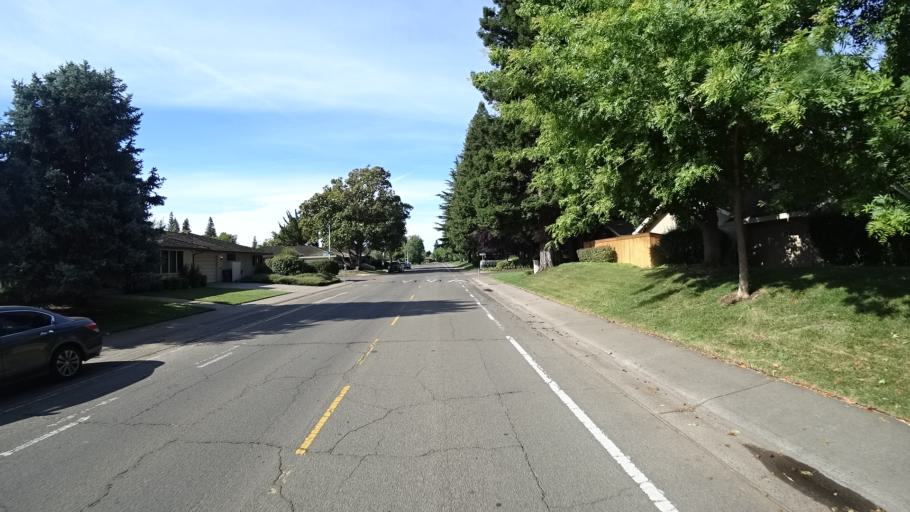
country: US
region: California
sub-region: Sacramento County
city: Rosemont
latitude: 38.5658
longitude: -121.4056
